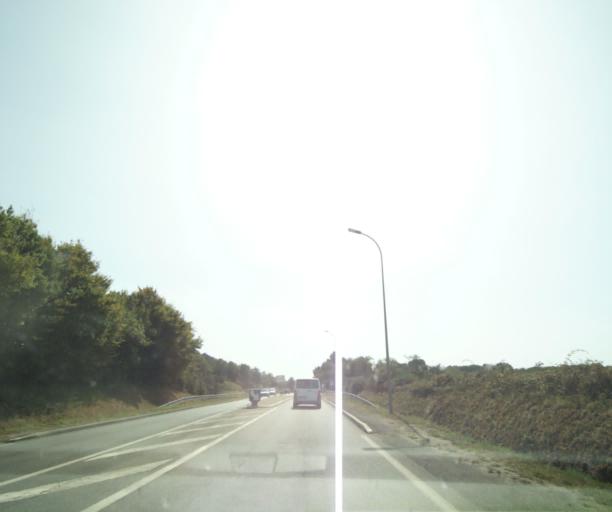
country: FR
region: Brittany
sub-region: Departement du Morbihan
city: Riantec
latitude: 47.7521
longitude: -3.2902
